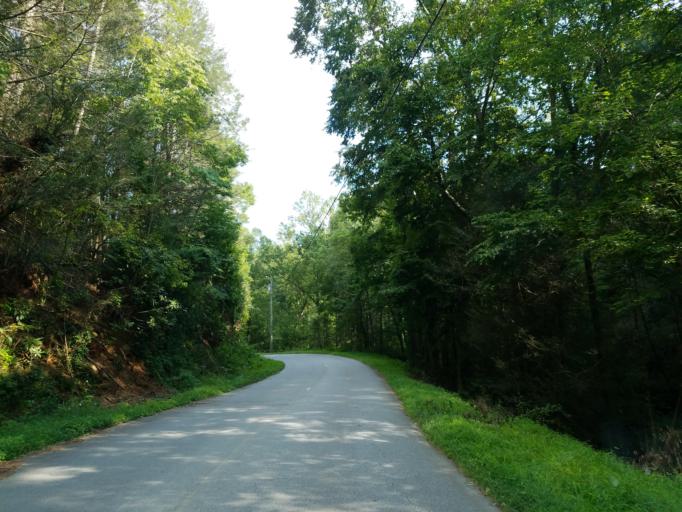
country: US
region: Georgia
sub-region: Fannin County
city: Blue Ridge
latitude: 34.7783
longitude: -84.3681
